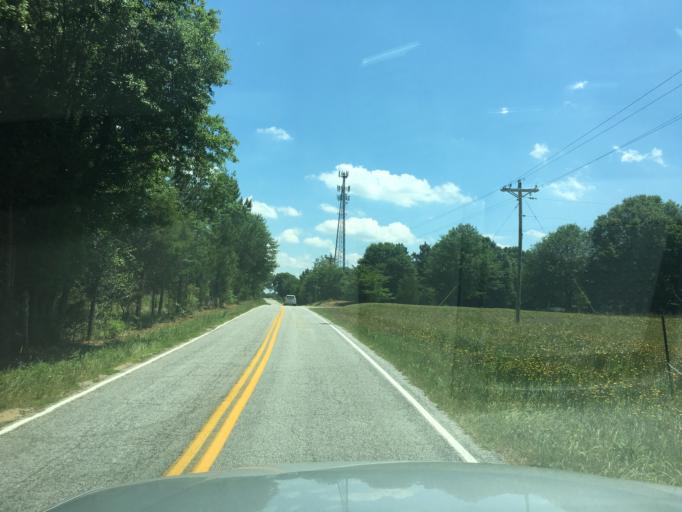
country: US
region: Georgia
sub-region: Hart County
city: Reed Creek
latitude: 34.5065
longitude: -82.9815
